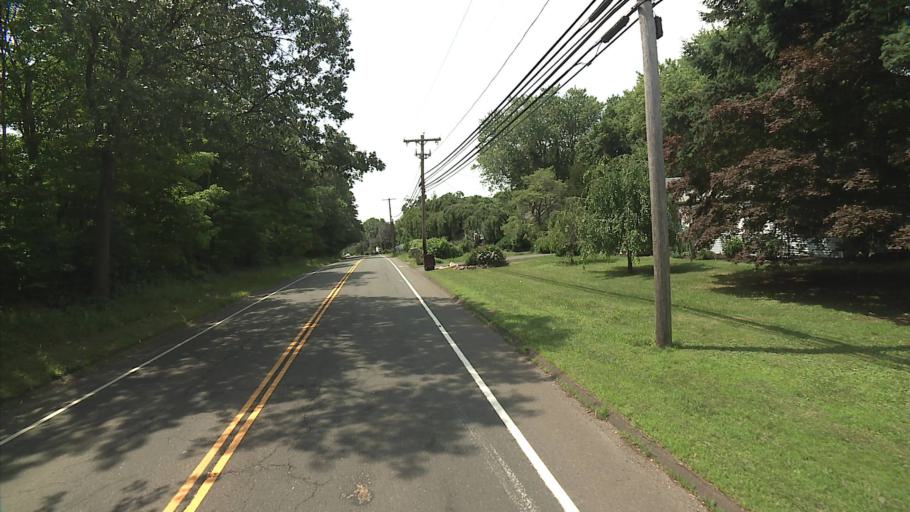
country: US
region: Connecticut
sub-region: New Haven County
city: North Branford
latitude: 41.3143
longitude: -72.7706
